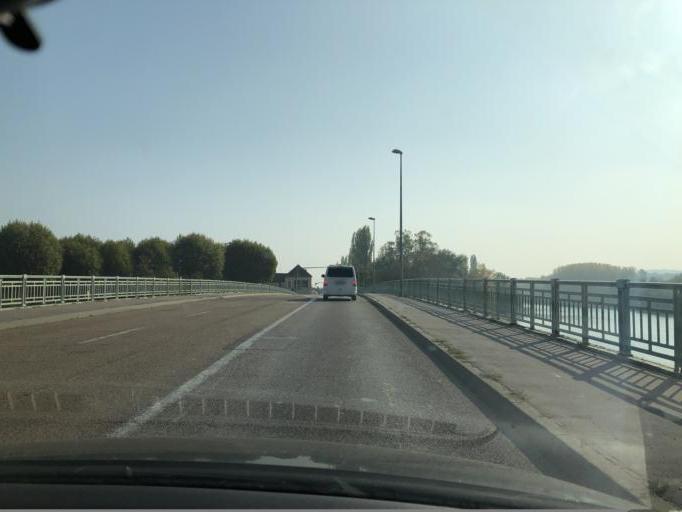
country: FR
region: Bourgogne
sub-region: Departement de l'Yonne
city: Pont-sur-Yonne
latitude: 48.2880
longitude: 3.2055
